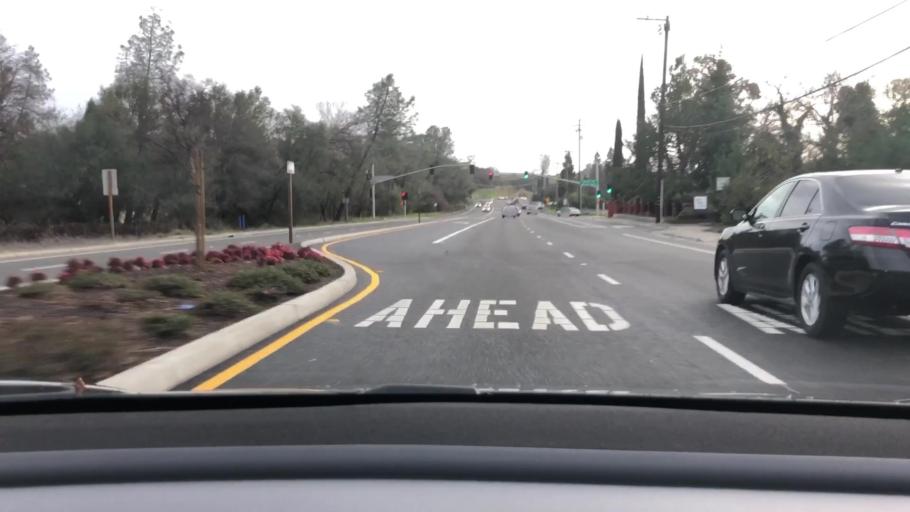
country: US
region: California
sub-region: Placer County
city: Granite Bay
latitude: 38.7372
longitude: -121.1706
